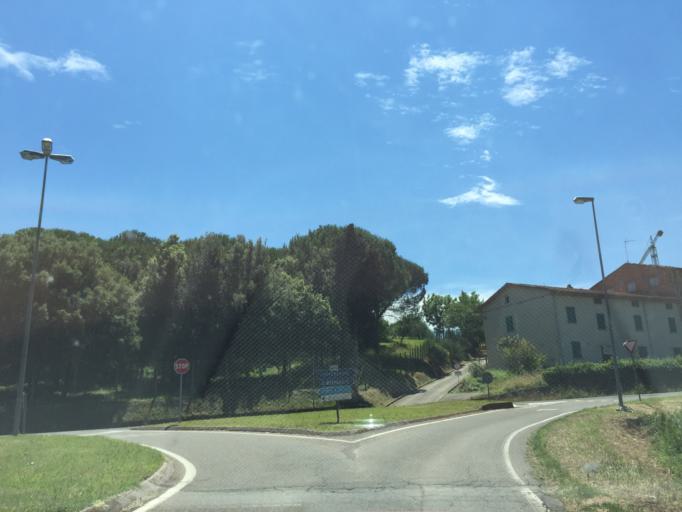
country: IT
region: Tuscany
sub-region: Province of Pisa
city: San Miniato
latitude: 43.6876
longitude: 10.7836
